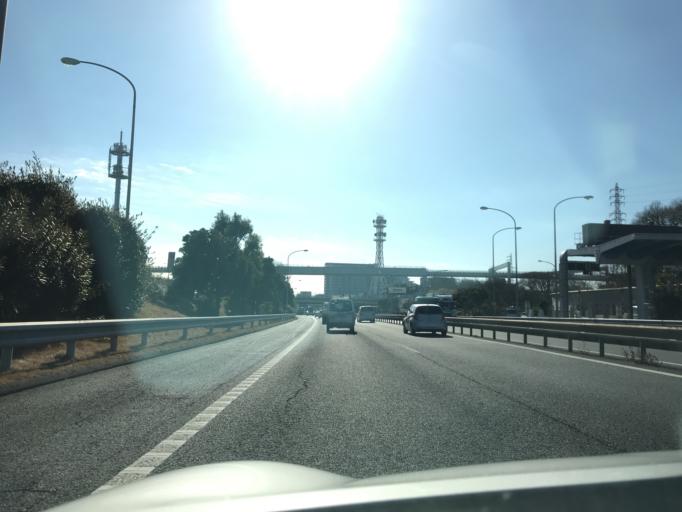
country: JP
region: Chiba
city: Chiba
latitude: 35.6435
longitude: 140.1122
